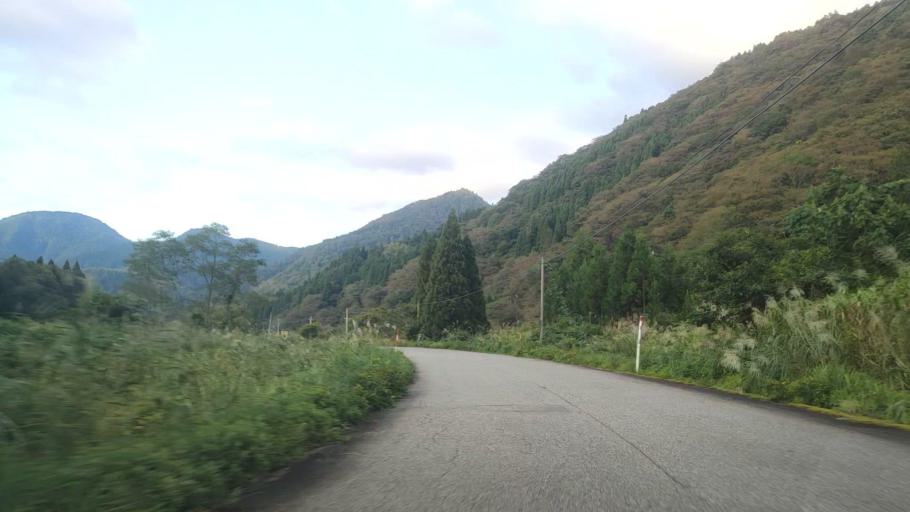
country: JP
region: Toyama
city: Yatsuomachi-higashikumisaka
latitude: 36.4655
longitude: 137.0858
